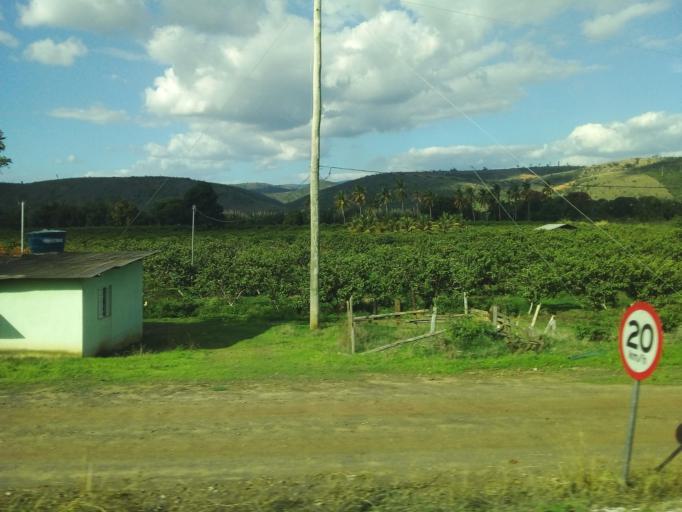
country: BR
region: Minas Gerais
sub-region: Conselheiro Pena
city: Conselheiro Pena
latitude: -19.1179
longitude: -41.5046
